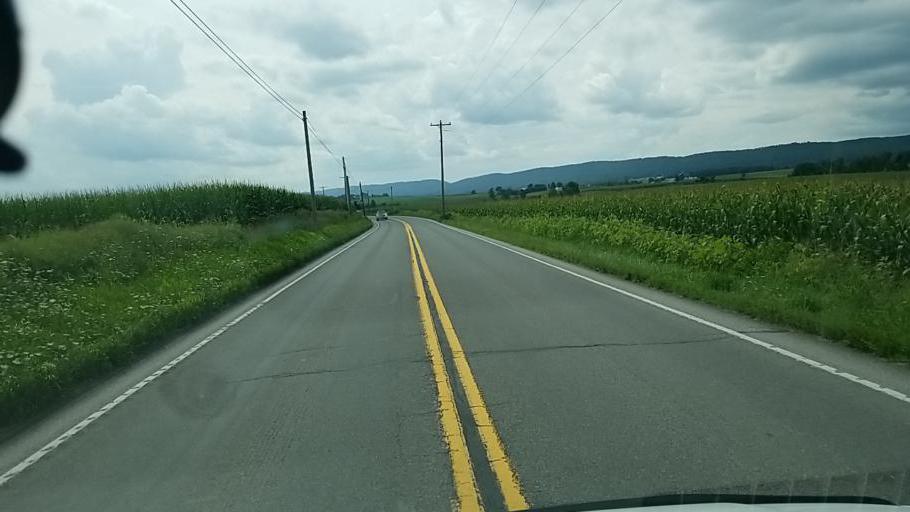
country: US
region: Pennsylvania
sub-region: Dauphin County
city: Elizabethville
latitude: 40.6060
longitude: -76.7845
